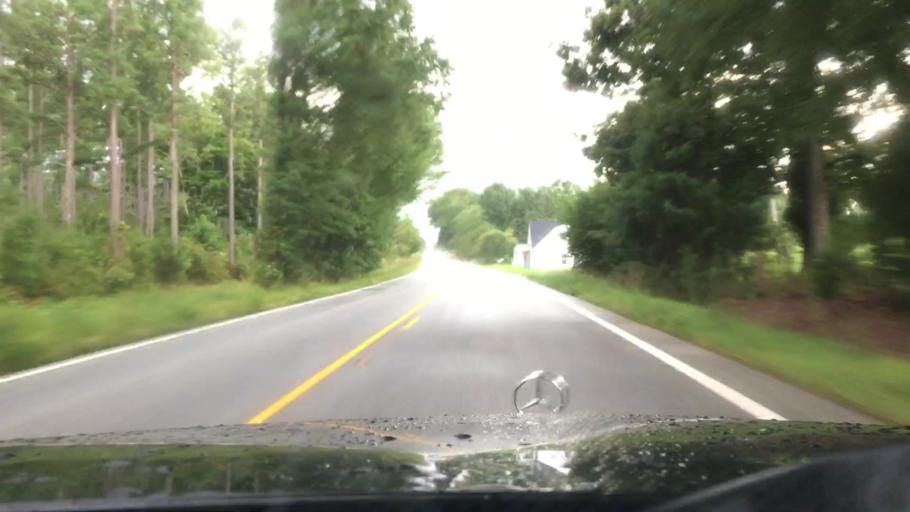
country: US
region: Virginia
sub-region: Nelson County
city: Lovingston
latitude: 37.7475
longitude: -78.9942
